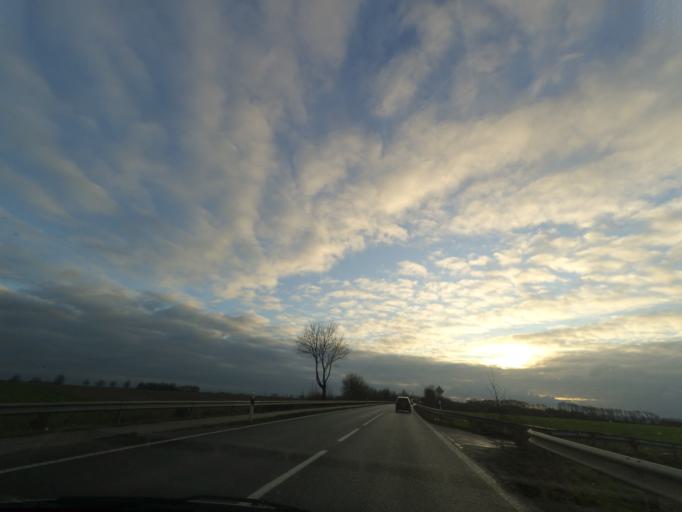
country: DE
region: North Rhine-Westphalia
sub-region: Regierungsbezirk Dusseldorf
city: Grevenbroich
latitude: 51.1119
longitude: 6.5586
